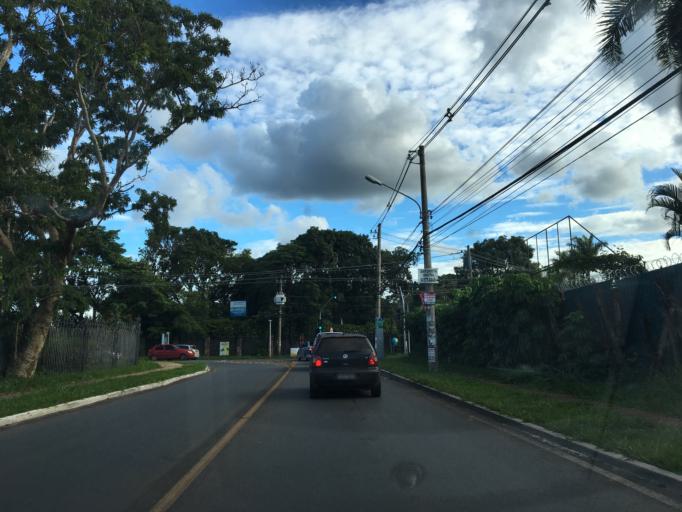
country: BR
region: Federal District
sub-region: Brasilia
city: Brasilia
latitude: -15.8471
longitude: -47.8900
